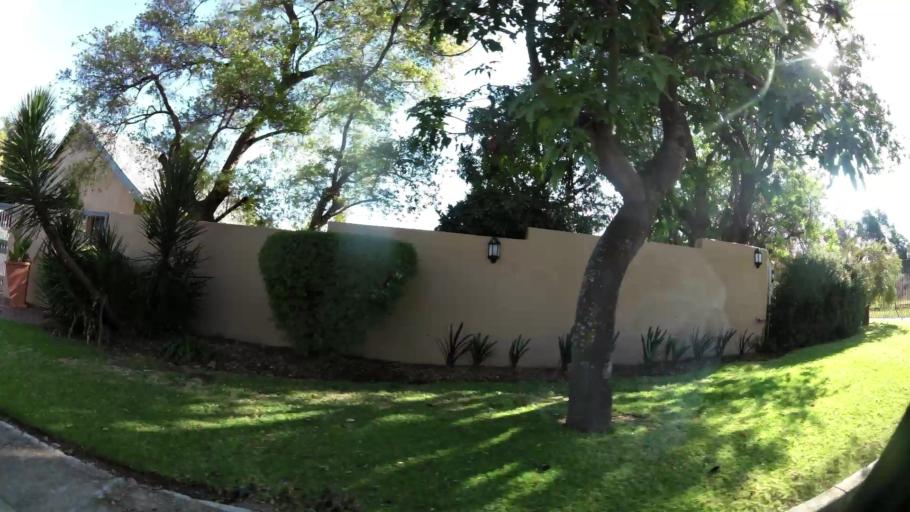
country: ZA
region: Gauteng
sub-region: City of Johannesburg Metropolitan Municipality
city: Roodepoort
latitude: -26.1007
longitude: 27.9563
